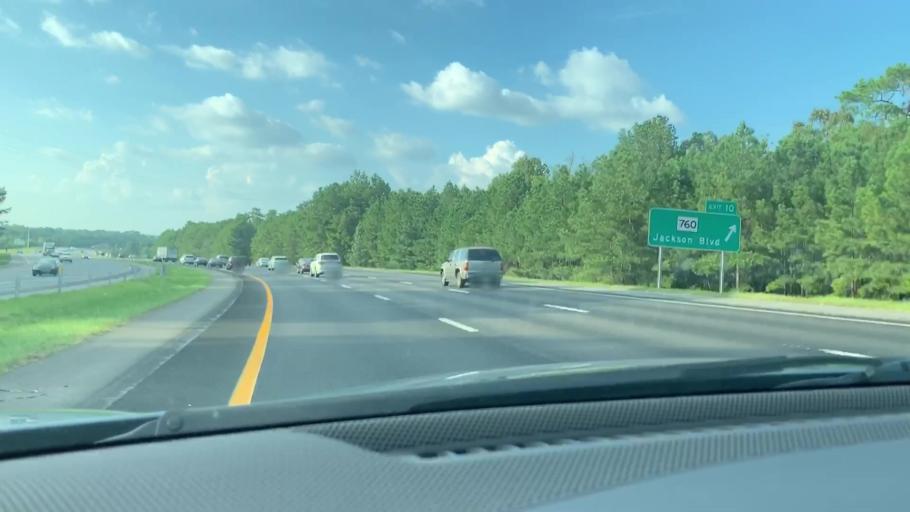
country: US
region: South Carolina
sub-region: Richland County
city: Forest Acres
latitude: 33.9903
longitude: -80.9535
